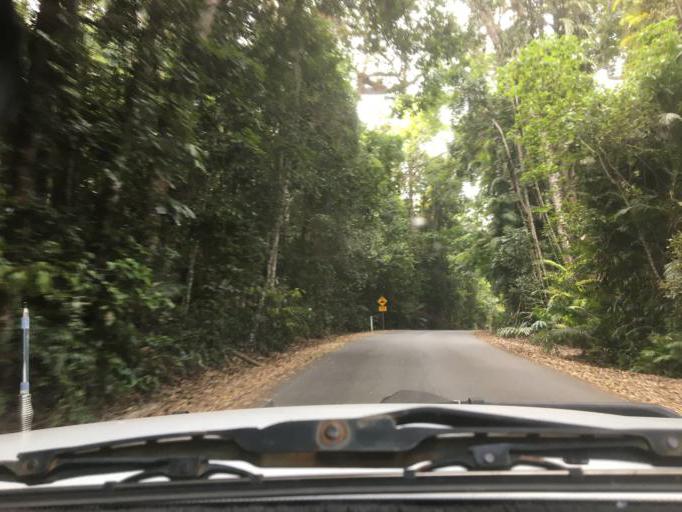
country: AU
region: Queensland
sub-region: Tablelands
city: Tolga
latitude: -17.2820
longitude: 145.6285
